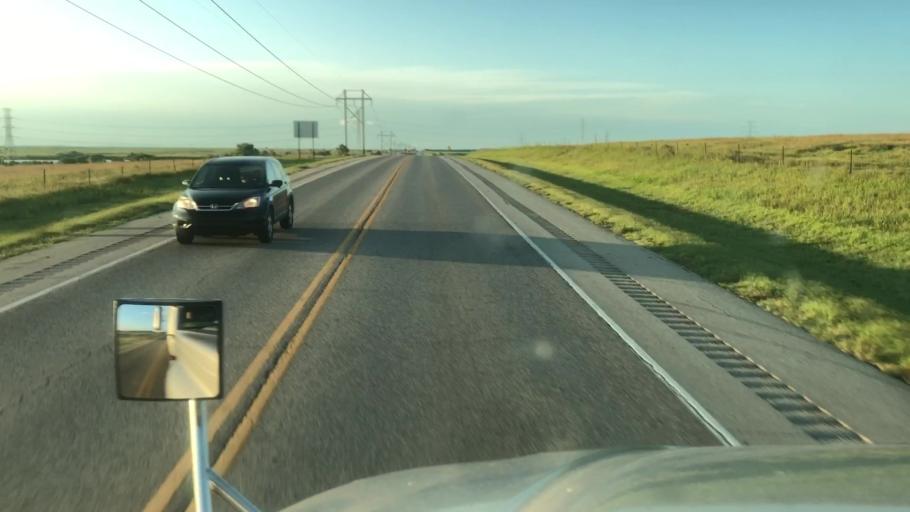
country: US
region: Oklahoma
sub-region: Noble County
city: Perry
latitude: 36.3952
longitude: -97.0676
